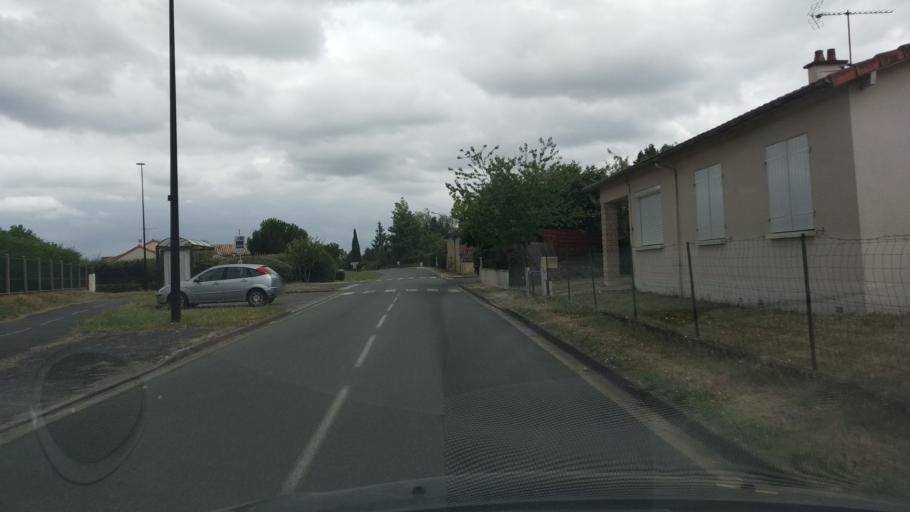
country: FR
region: Poitou-Charentes
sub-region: Departement de la Vienne
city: Smarves
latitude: 46.5084
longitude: 0.3568
